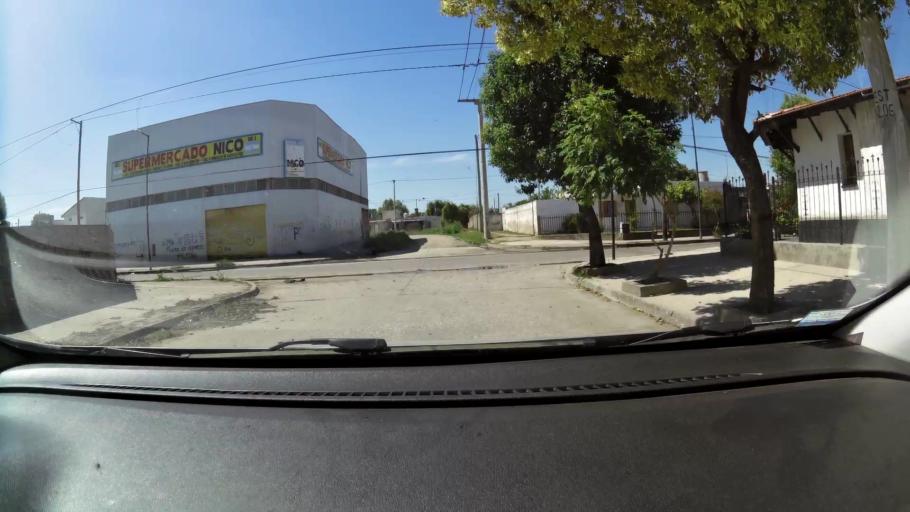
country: AR
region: Cordoba
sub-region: Departamento de Capital
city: Cordoba
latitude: -31.3674
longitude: -64.1429
